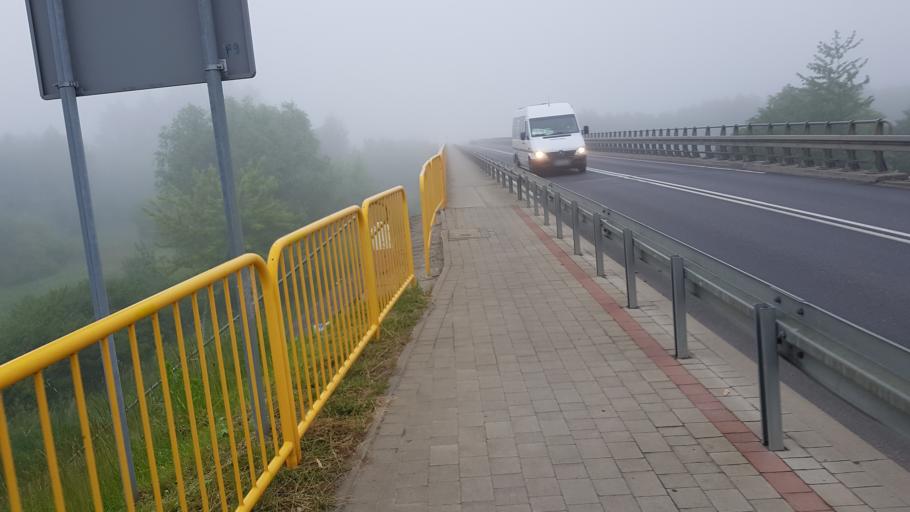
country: PL
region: Subcarpathian Voivodeship
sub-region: Powiat stalowowolski
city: Stalowa Wola
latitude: 50.6111
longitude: 22.0592
